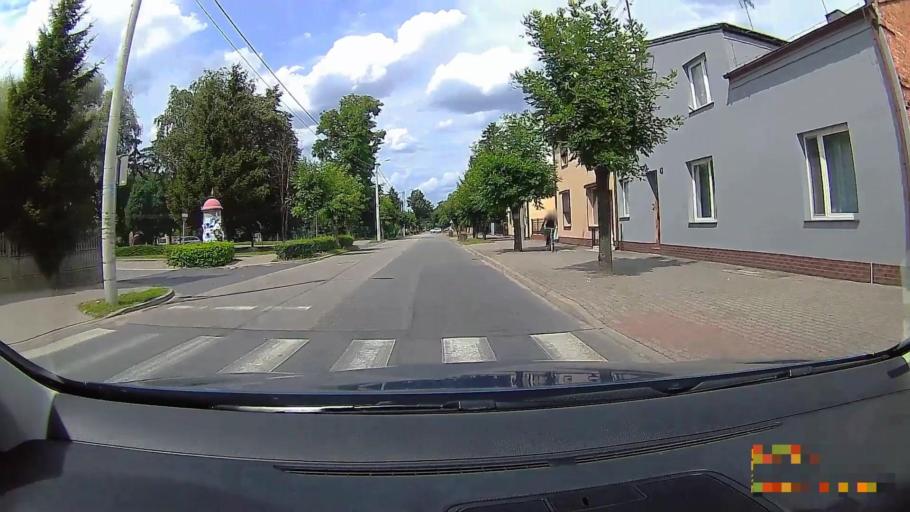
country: PL
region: Greater Poland Voivodeship
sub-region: Powiat koninski
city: Rychwal
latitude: 52.0724
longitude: 18.1644
